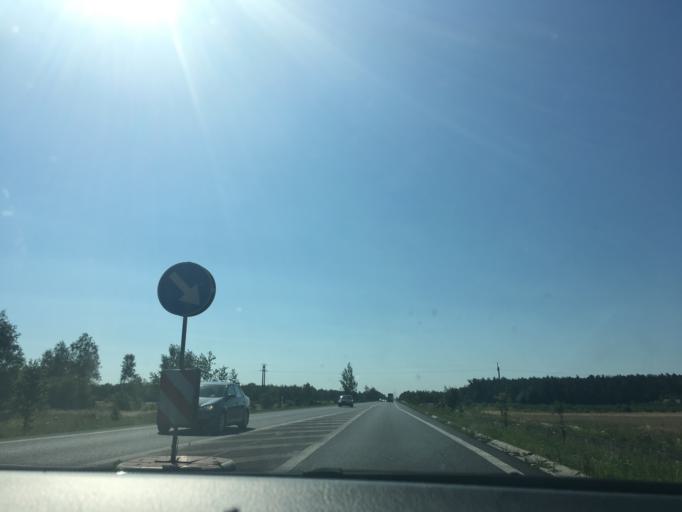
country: PL
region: Lublin Voivodeship
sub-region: Powiat lubartowski
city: Lubartow
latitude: 51.4509
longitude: 22.5794
